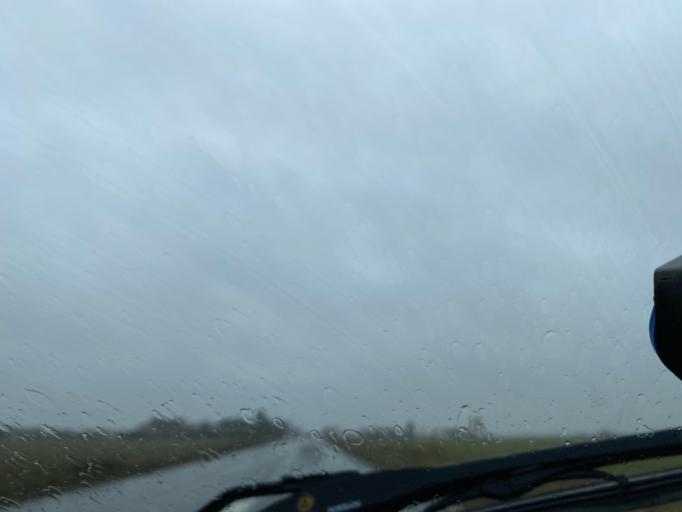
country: FR
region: Centre
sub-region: Departement d'Eure-et-Loir
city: Le Coudray
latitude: 48.4192
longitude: 1.5285
